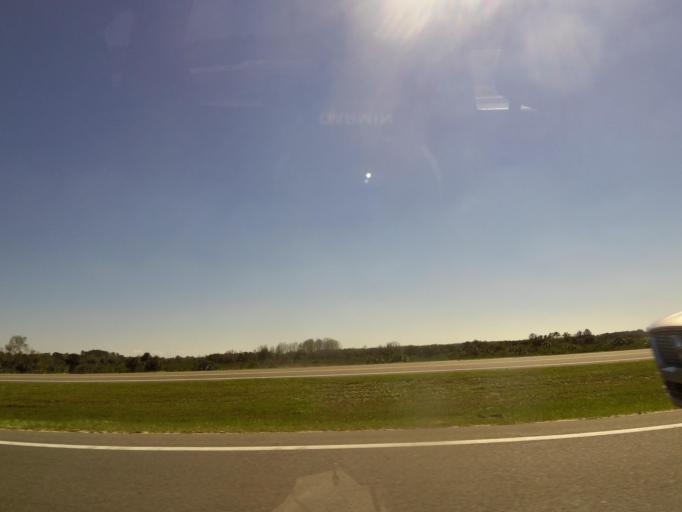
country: US
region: Florida
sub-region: Seminole County
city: Heathrow
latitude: 28.8125
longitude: -81.4374
